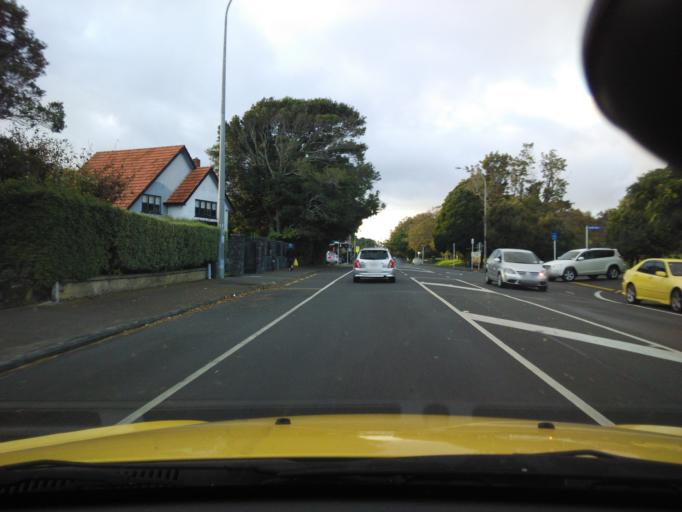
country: NZ
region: Auckland
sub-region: Auckland
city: Auckland
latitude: -36.9083
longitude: 174.7752
